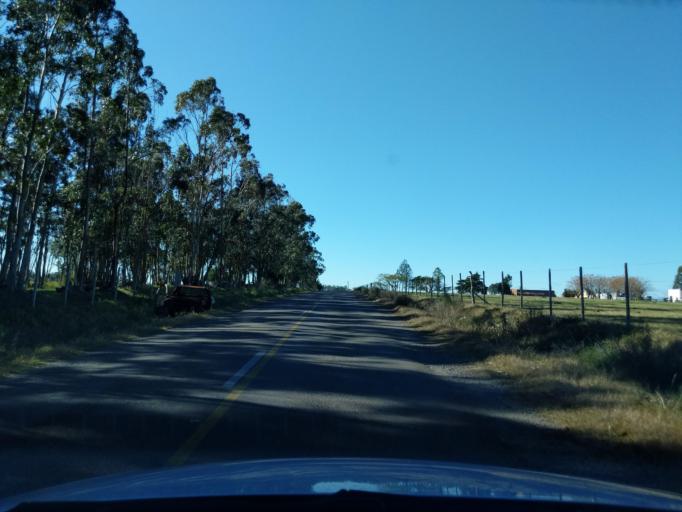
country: UY
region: Florida
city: Florida
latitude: -34.0514
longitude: -56.2482
